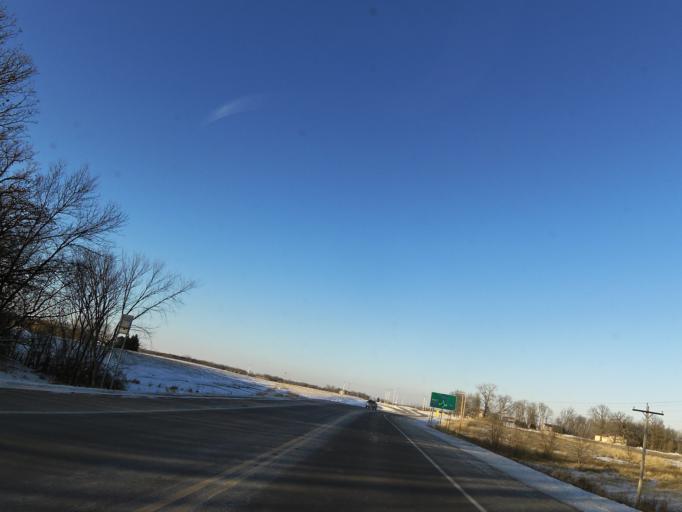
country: US
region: Minnesota
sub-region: Rice County
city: Lonsdale
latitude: 44.5402
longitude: -93.4428
